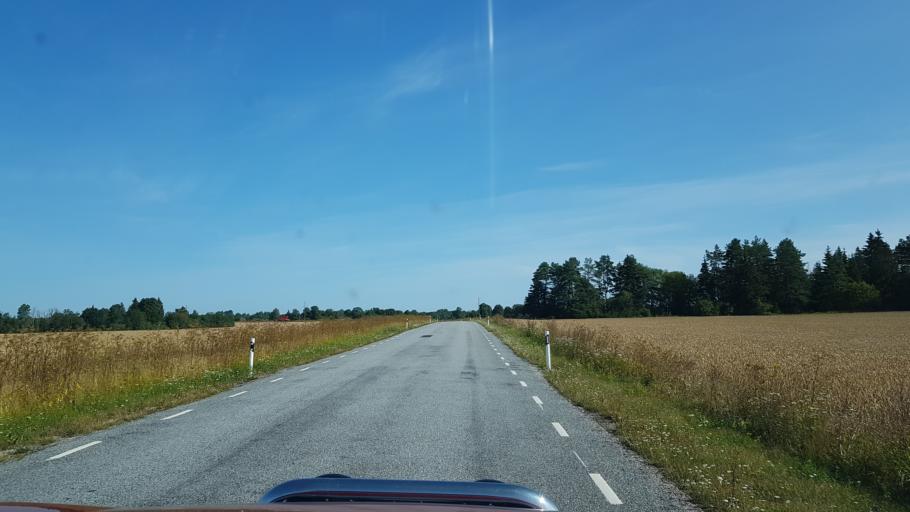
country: EE
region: Harju
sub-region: Raasiku vald
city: Raasiku
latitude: 59.2918
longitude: 25.1693
